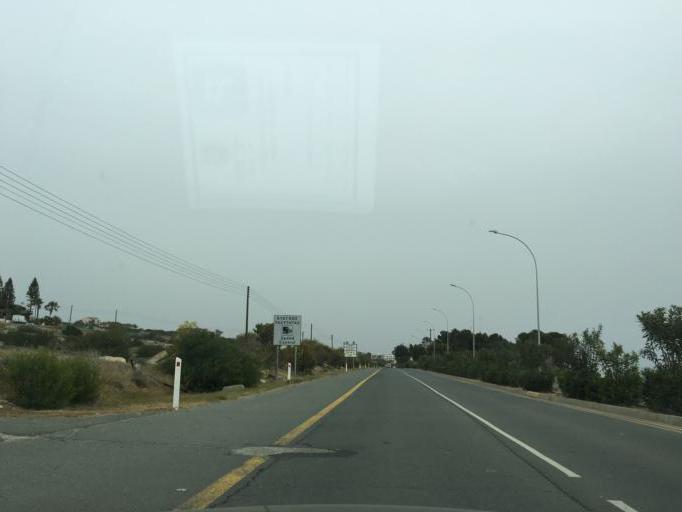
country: CY
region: Ammochostos
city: Ayia Napa
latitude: 34.9916
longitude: 34.0038
